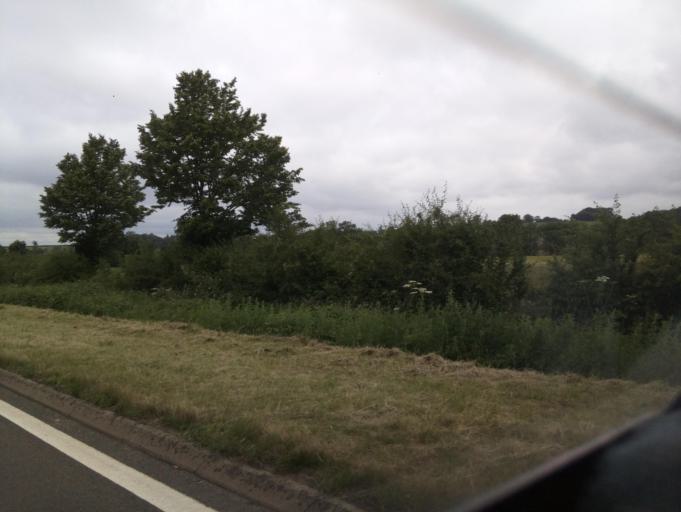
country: GB
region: England
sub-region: Leicestershire
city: Houghton on the Hill
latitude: 52.6202
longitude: -0.9591
